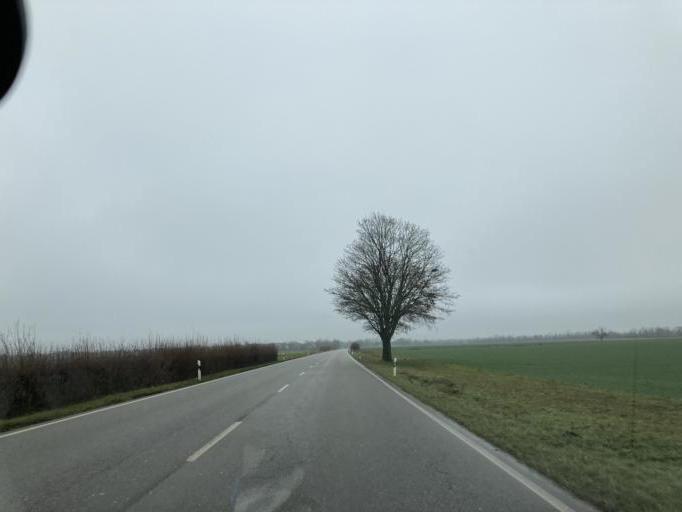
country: DE
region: Baden-Wuerttemberg
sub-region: Freiburg Region
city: Neuenburg am Rhein
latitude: 47.8170
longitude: 7.5823
